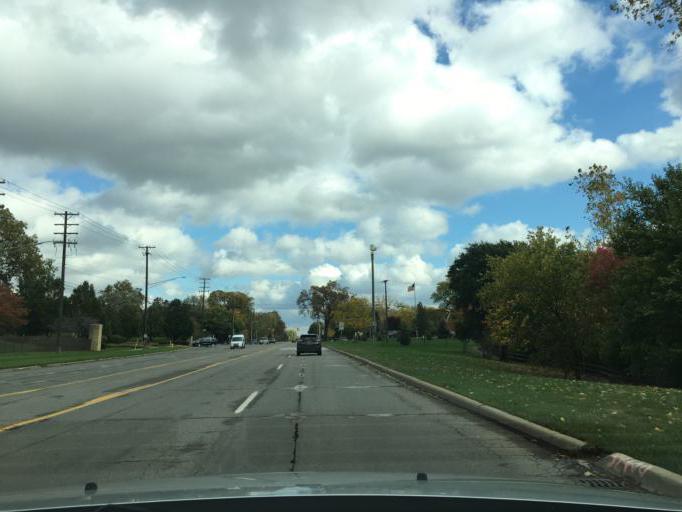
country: US
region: Michigan
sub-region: Wayne County
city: Dearborn
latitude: 42.3023
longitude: -83.1961
